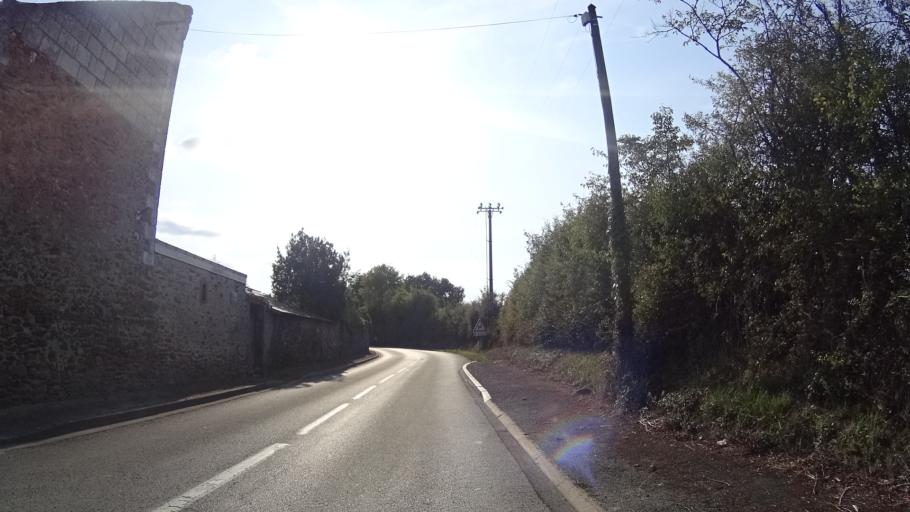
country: FR
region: Pays de la Loire
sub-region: Departement de Maine-et-Loire
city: Savennieres
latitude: 47.3966
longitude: -0.6369
